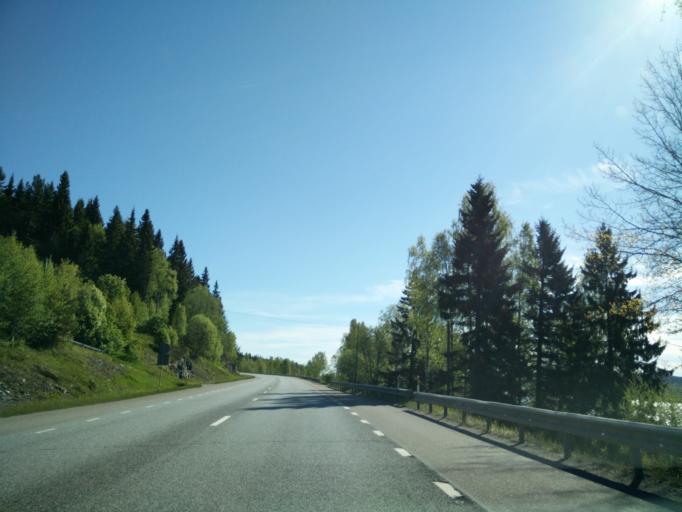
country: SE
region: Vaesternorrland
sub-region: Kramfors Kommun
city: Nordingra
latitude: 63.0045
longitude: 18.2569
